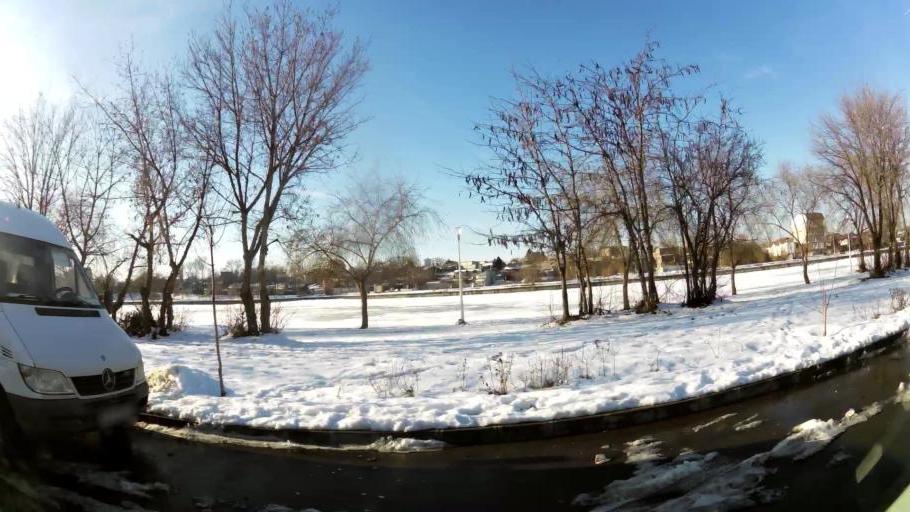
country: RO
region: Ilfov
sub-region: Comuna Fundeni-Dobroesti
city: Fundeni
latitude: 44.4697
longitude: 26.1314
